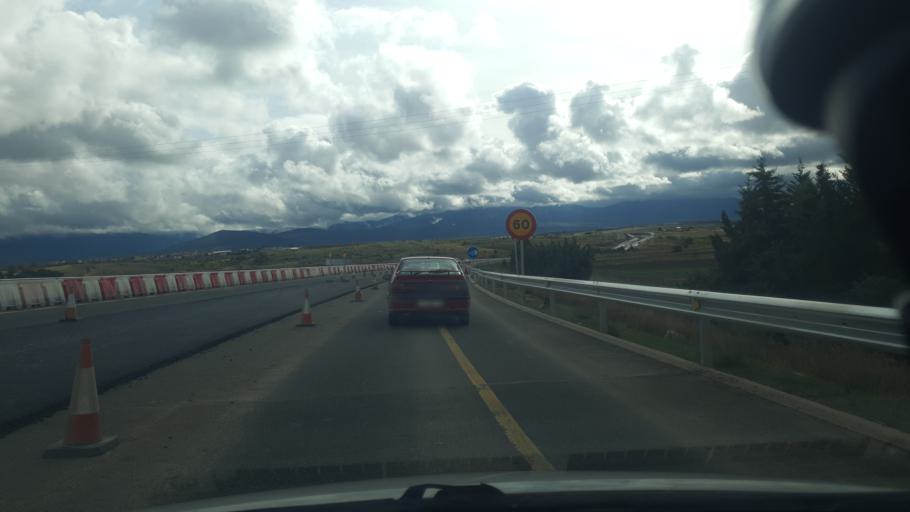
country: ES
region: Castille and Leon
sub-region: Provincia de Segovia
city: La Lastrilla
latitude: 40.9701
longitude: -4.0855
